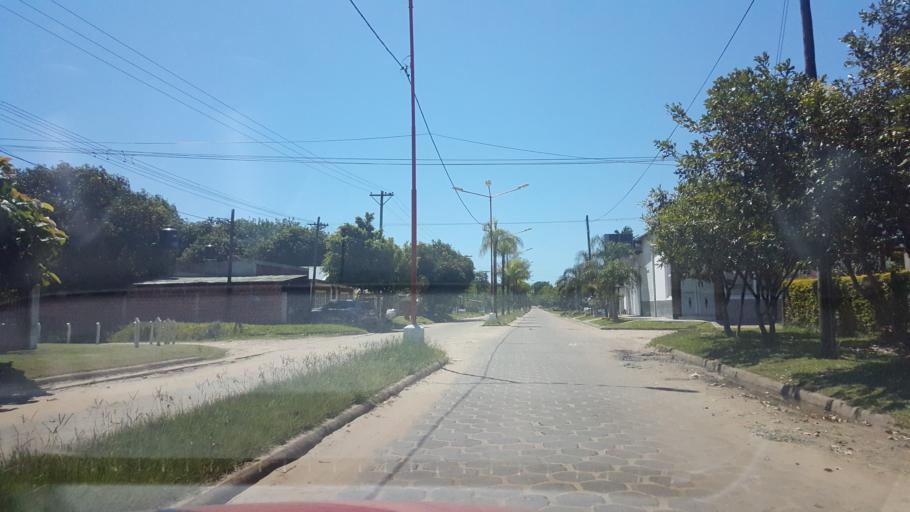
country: AR
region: Corrientes
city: Ituzaingo
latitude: -27.5948
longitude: -56.6980
